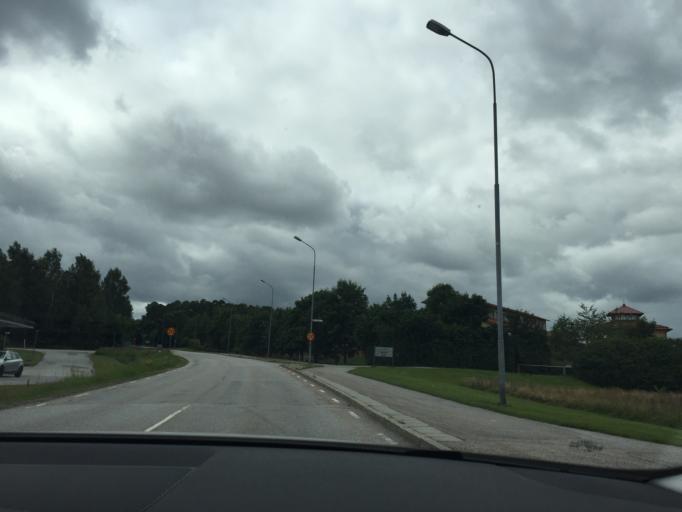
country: SE
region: Skane
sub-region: Sjobo Kommun
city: Blentarp
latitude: 55.5838
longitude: 13.6023
